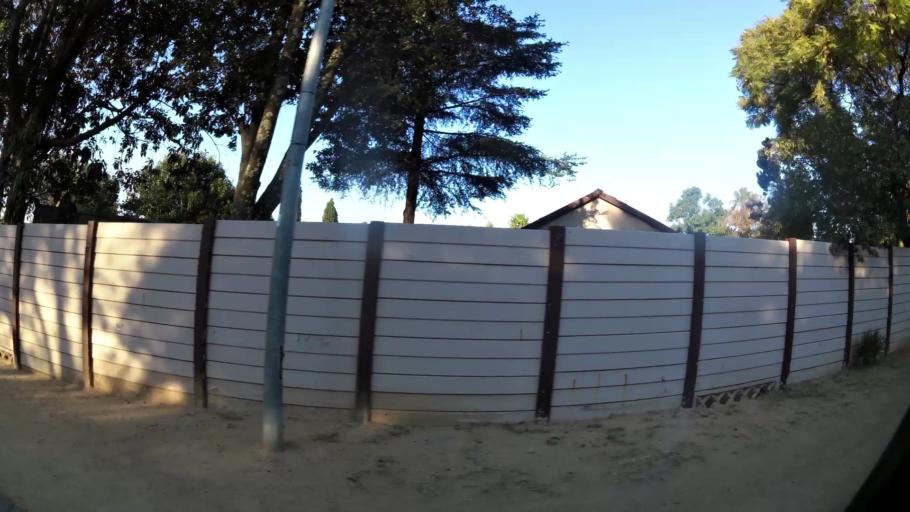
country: ZA
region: Gauteng
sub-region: City of Johannesburg Metropolitan Municipality
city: Diepsloot
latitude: -26.0415
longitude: 27.9770
